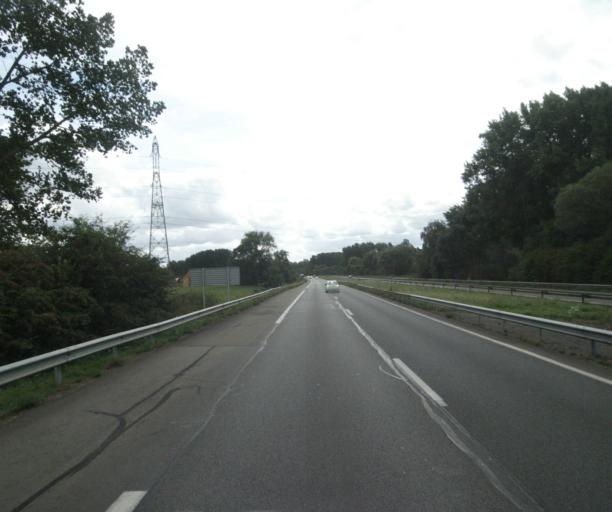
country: FR
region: Nord-Pas-de-Calais
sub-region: Departement du Nord
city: Sainghin-en-Melantois
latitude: 50.5575
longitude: 3.1749
